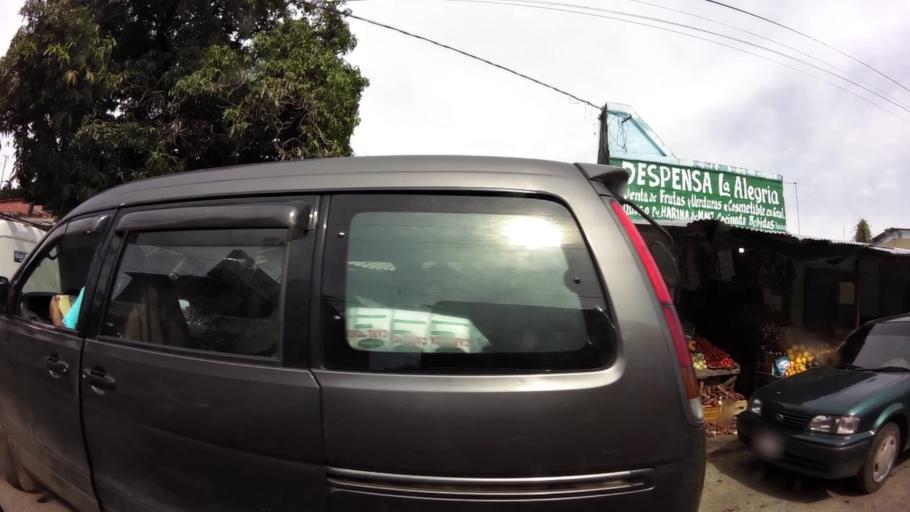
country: PY
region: Central
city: Limpio
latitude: -25.1689
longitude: -57.4747
